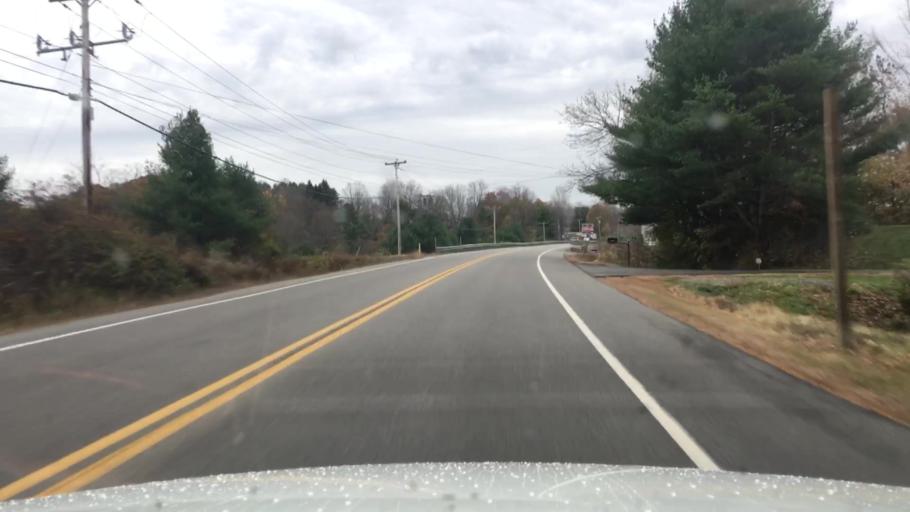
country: US
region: Maine
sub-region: Kennebec County
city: Pittston
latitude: 44.2206
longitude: -69.7566
